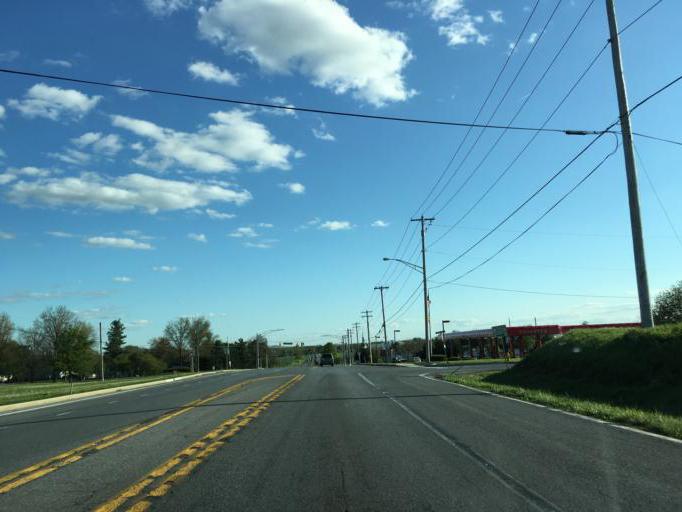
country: US
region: Maryland
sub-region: Frederick County
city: Walkersville
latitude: 39.4654
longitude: -77.3641
